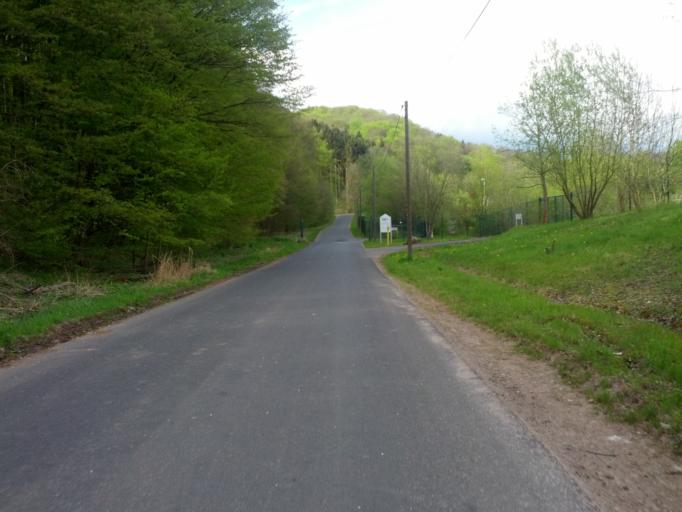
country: DE
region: Thuringia
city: Krauthausen
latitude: 50.9965
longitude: 10.2405
